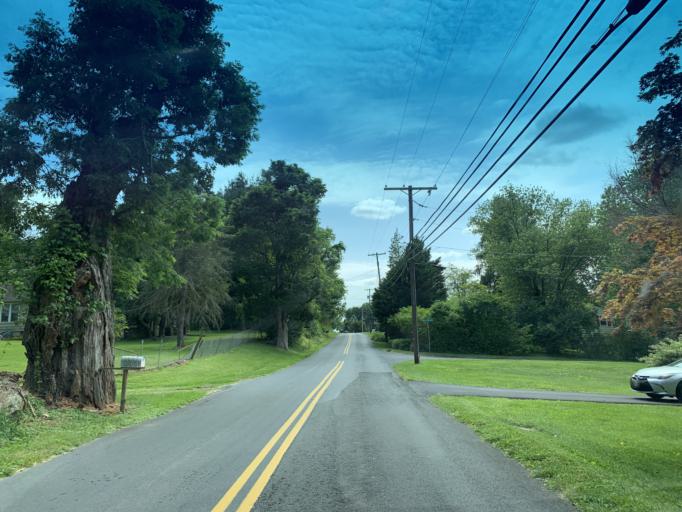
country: US
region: Maryland
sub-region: Harford County
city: Jarrettsville
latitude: 39.6315
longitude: -76.4617
